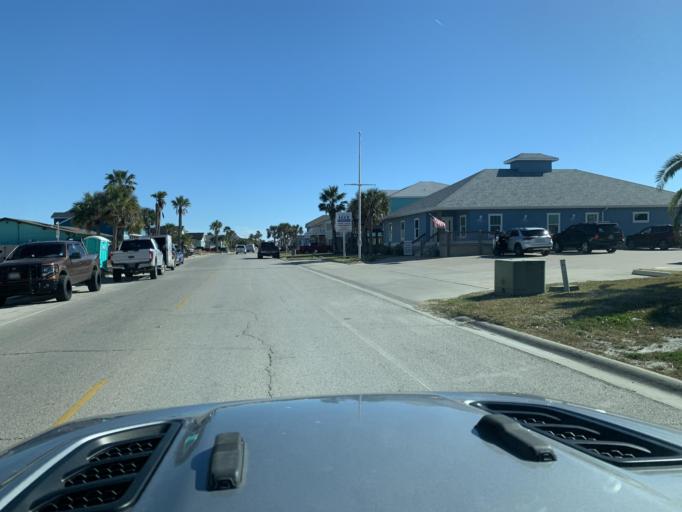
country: US
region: Texas
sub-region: Aransas County
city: Fulton
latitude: 28.0483
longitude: -97.0296
